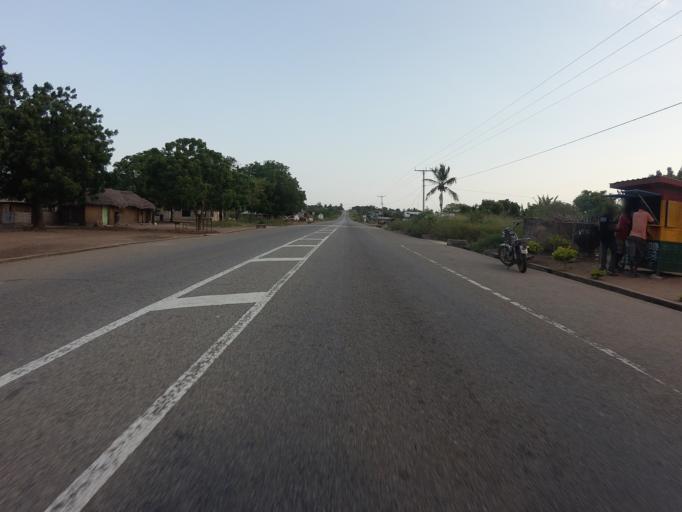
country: GH
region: Volta
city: Anloga
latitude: 6.0589
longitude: 0.6045
